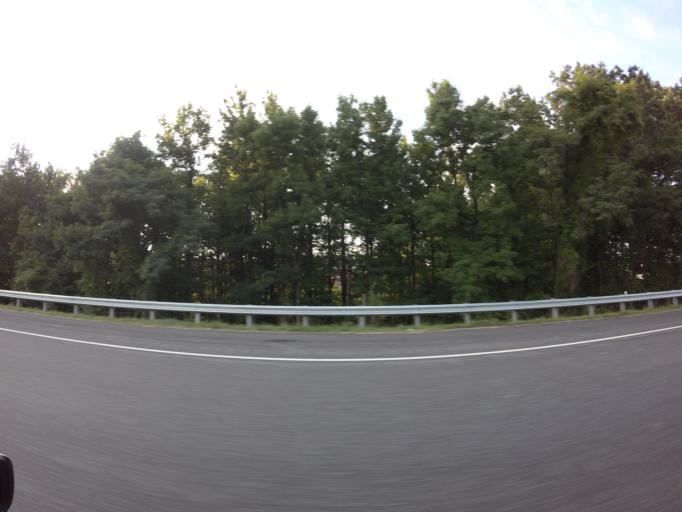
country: US
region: Maryland
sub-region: Howard County
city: North Laurel
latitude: 39.1343
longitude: -76.8556
